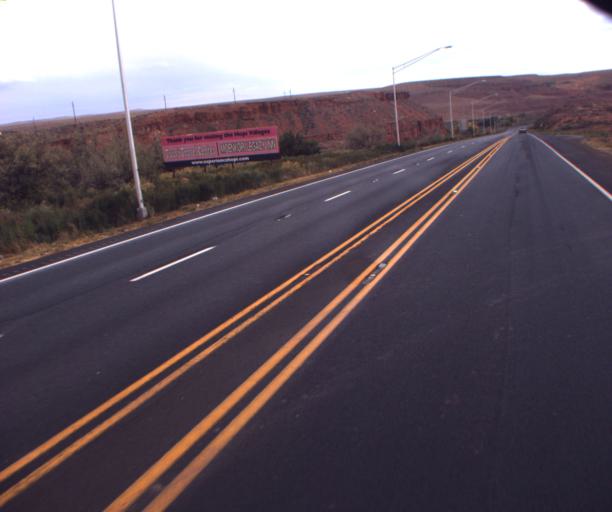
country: US
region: Arizona
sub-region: Coconino County
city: Tuba City
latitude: 36.1165
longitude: -111.2318
